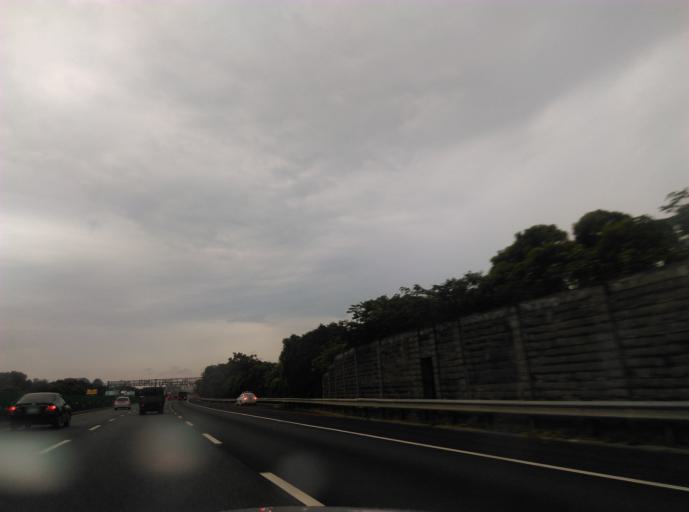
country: TW
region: Taiwan
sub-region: Hsinchu
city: Hsinchu
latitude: 24.7128
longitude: 120.8913
